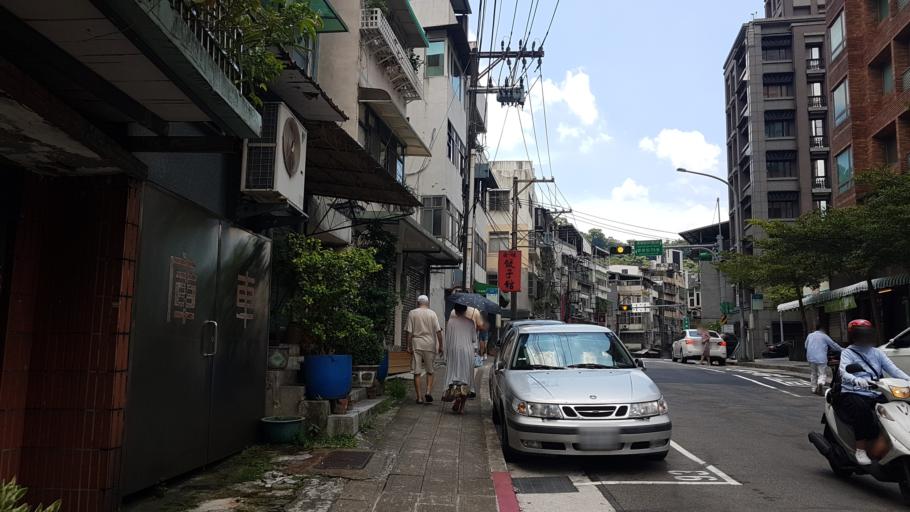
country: TW
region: Taipei
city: Taipei
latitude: 24.9977
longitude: 121.5480
